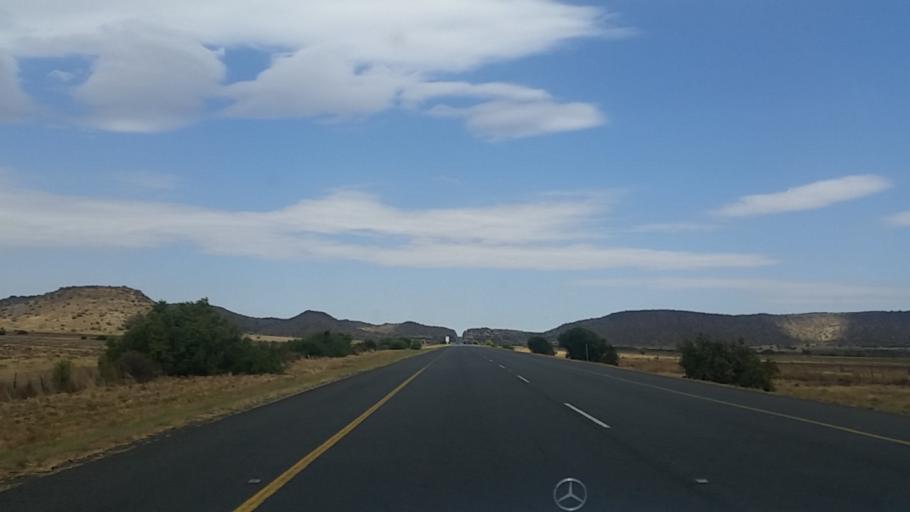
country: ZA
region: Northern Cape
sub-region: Pixley ka Seme District Municipality
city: Colesberg
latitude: -30.6345
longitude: 25.2406
